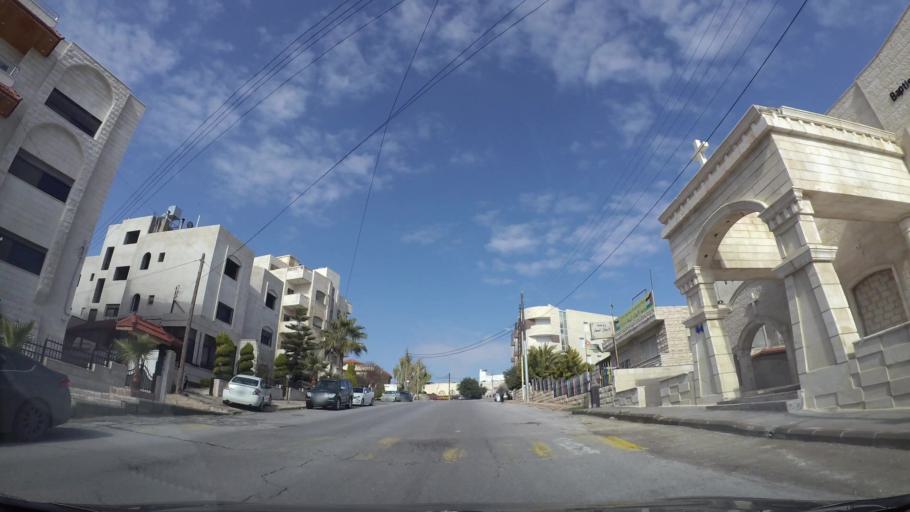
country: JO
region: Amman
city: Al Jubayhah
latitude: 32.0013
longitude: 35.8873
